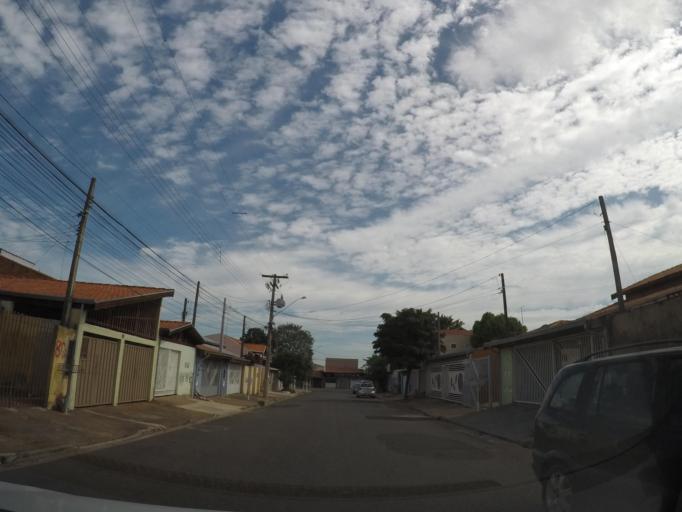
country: BR
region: Sao Paulo
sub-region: Hortolandia
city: Hortolandia
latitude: -22.8315
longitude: -47.1872
